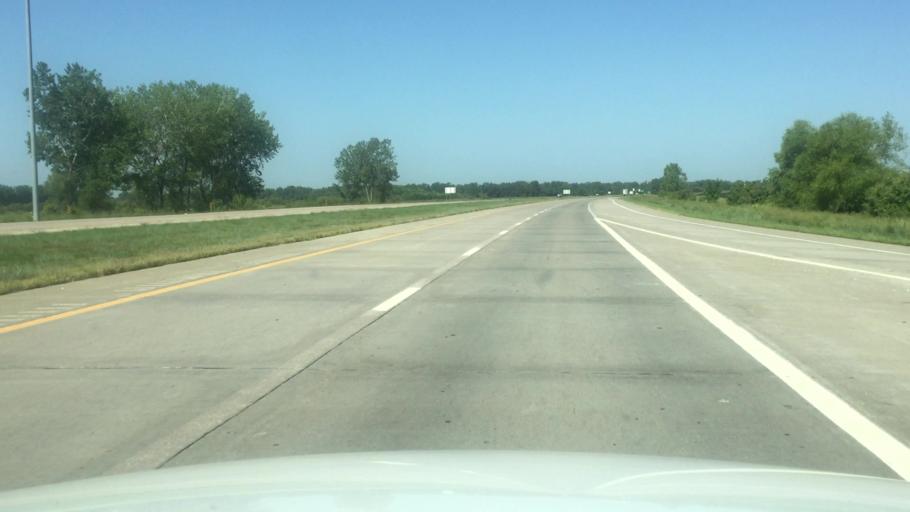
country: US
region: Kansas
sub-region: Doniphan County
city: Elwood
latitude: 39.7408
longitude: -94.8972
